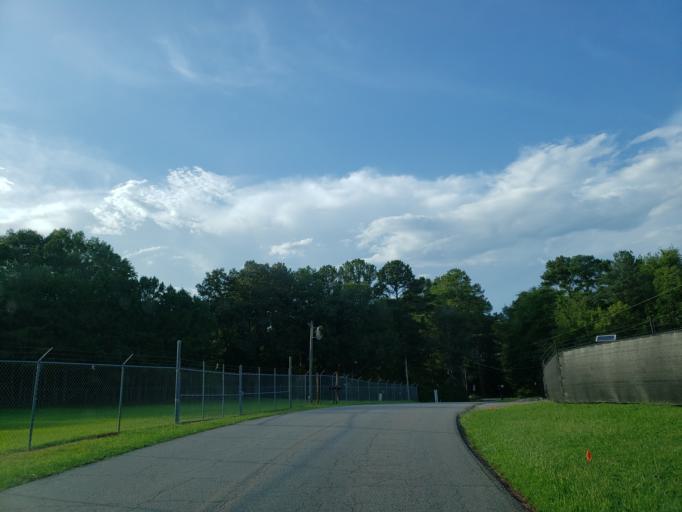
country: US
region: Georgia
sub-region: Bartow County
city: Euharlee
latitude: 34.2362
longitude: -84.9544
